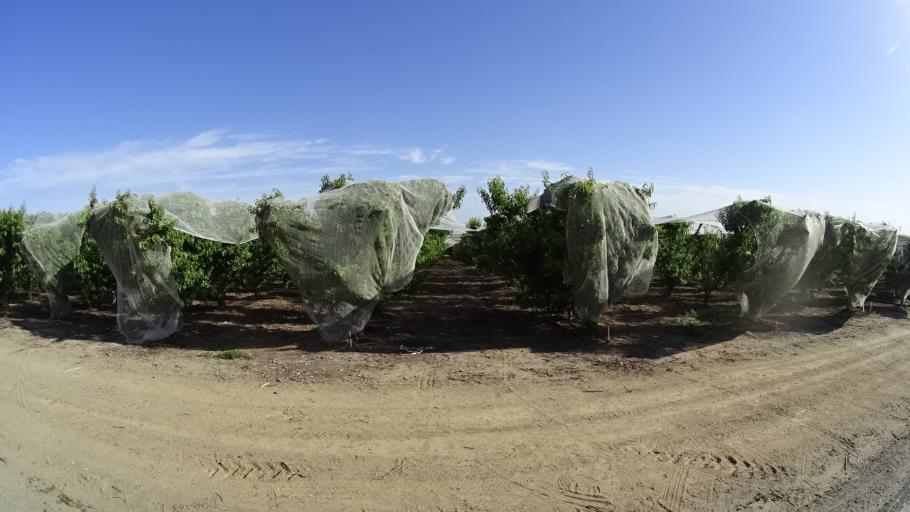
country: US
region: California
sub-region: Kings County
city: Kettleman City
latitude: 36.0095
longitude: -119.9817
